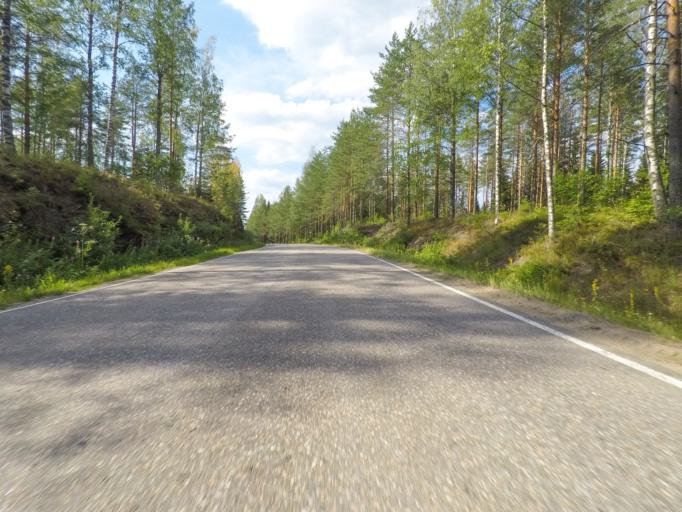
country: FI
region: Southern Savonia
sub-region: Mikkeli
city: Puumala
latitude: 61.6846
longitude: 28.2291
